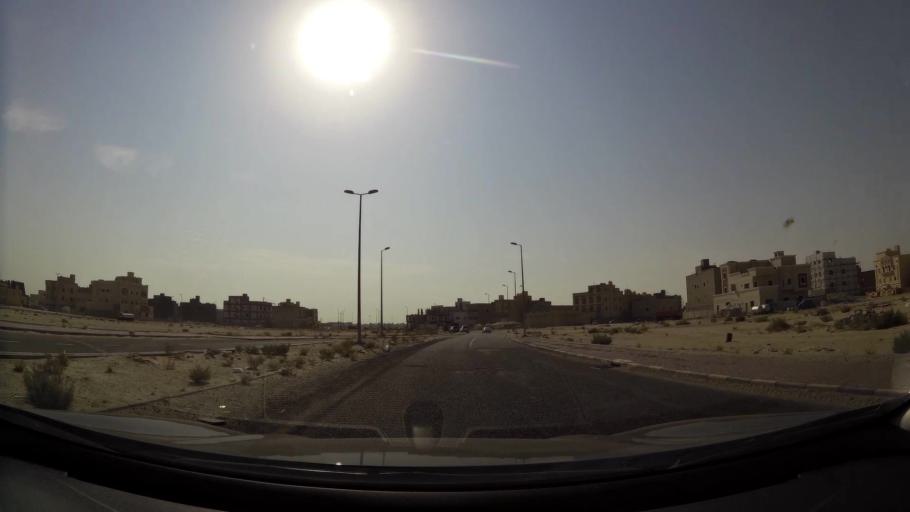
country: KW
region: Al Ahmadi
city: Al Wafrah
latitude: 28.7855
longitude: 48.0489
